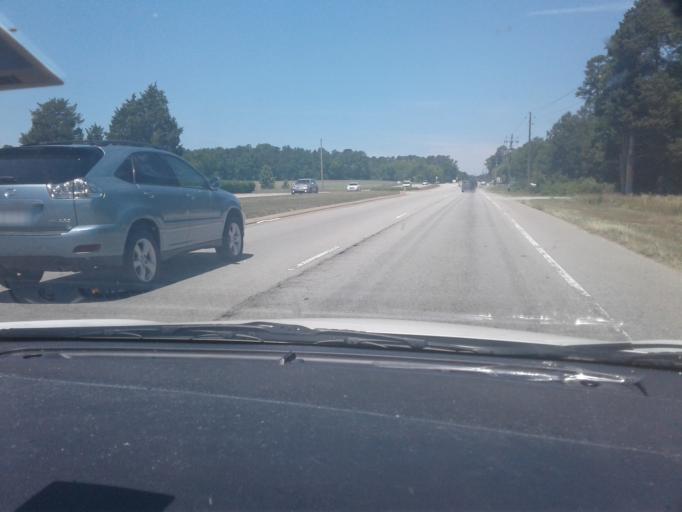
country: US
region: North Carolina
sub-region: Wake County
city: Holly Springs
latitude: 35.6256
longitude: -78.8205
